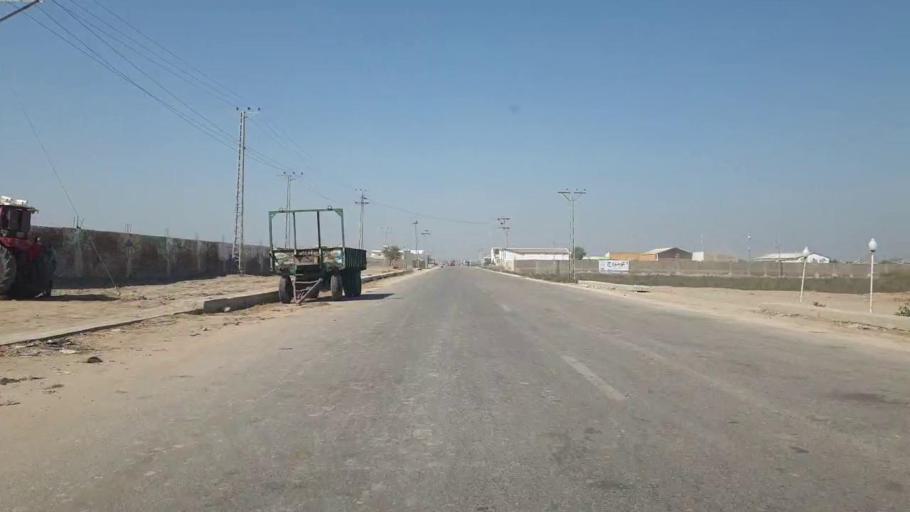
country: PK
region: Sindh
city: Talhar
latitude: 24.8752
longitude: 68.8153
